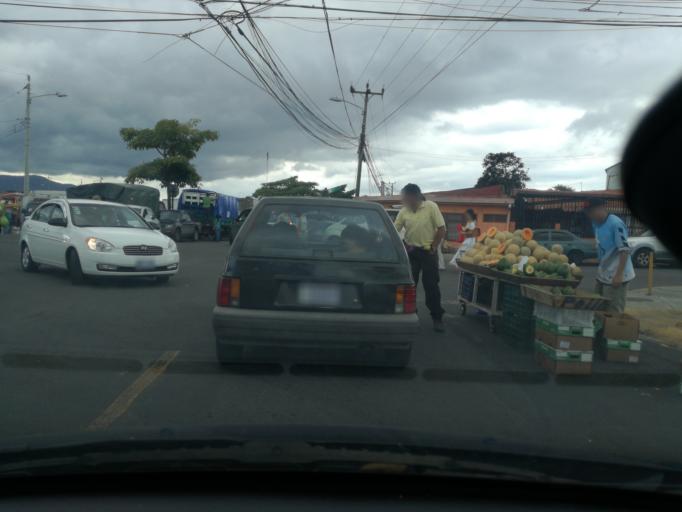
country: CR
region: San Jose
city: San Pedro
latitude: 9.9182
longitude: -84.0510
